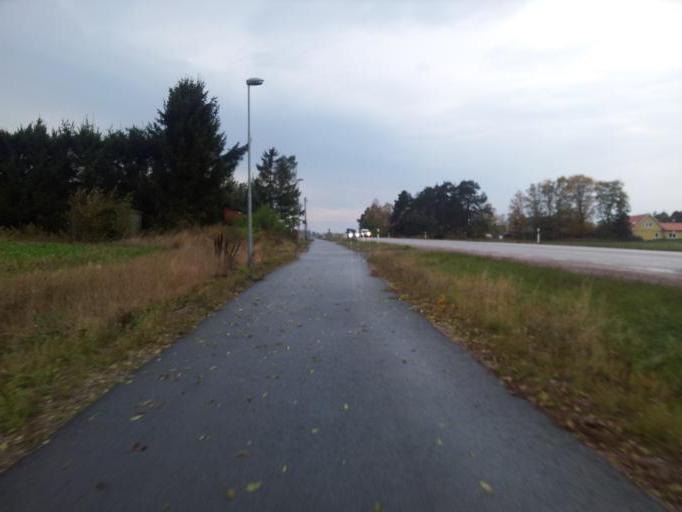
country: SE
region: Uppsala
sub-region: Uppsala Kommun
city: Gamla Uppsala
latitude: 59.8944
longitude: 17.7040
